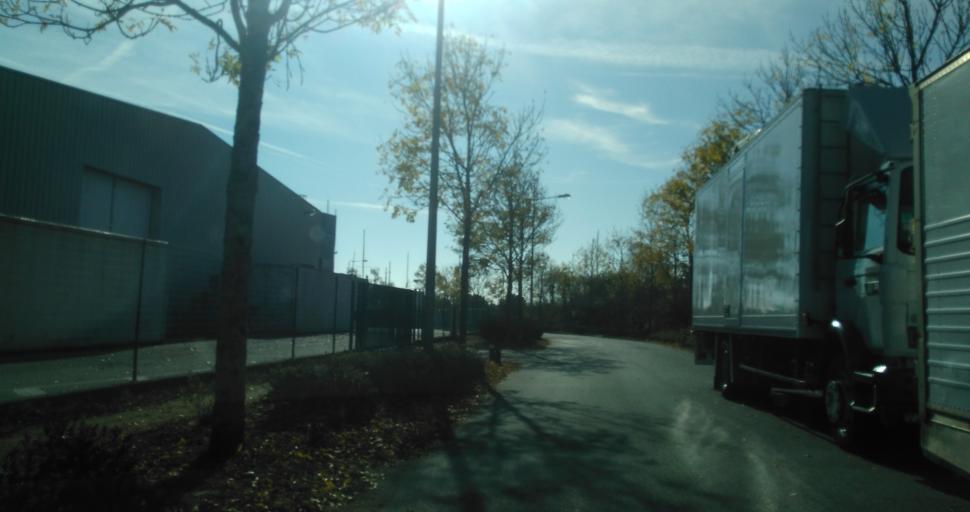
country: FR
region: Brittany
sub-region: Departement du Morbihan
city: Sene
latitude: 47.6343
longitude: -2.7638
